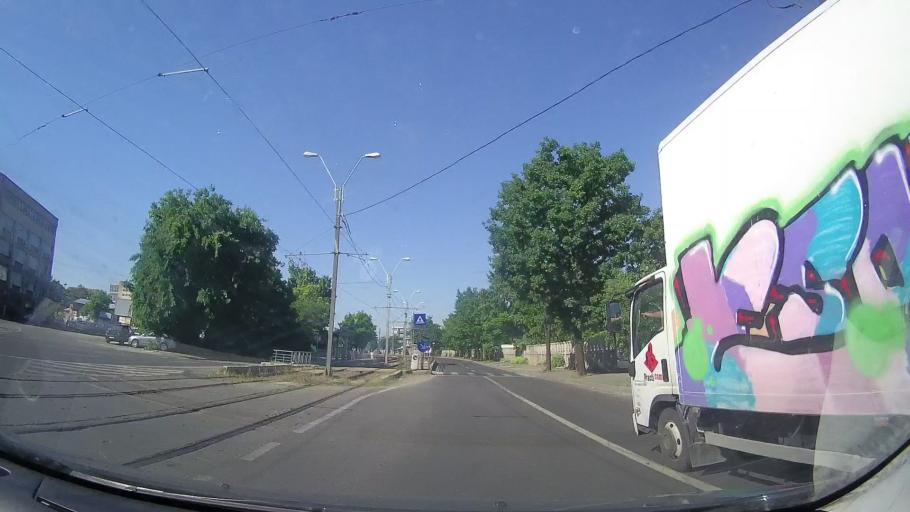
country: RO
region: Bucuresti
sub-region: Municipiul Bucuresti
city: Bucuresti
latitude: 44.4150
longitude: 26.0920
